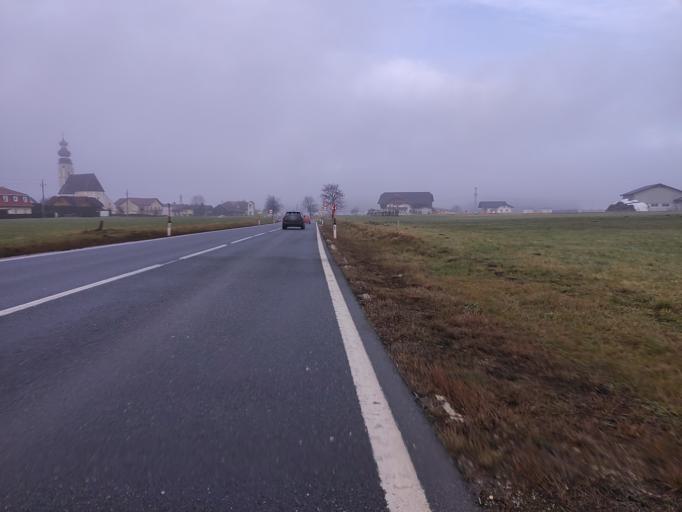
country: AT
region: Upper Austria
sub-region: Politischer Bezirk Vocklabruck
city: Oberhofen am Irrsee
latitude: 47.9668
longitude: 13.2855
